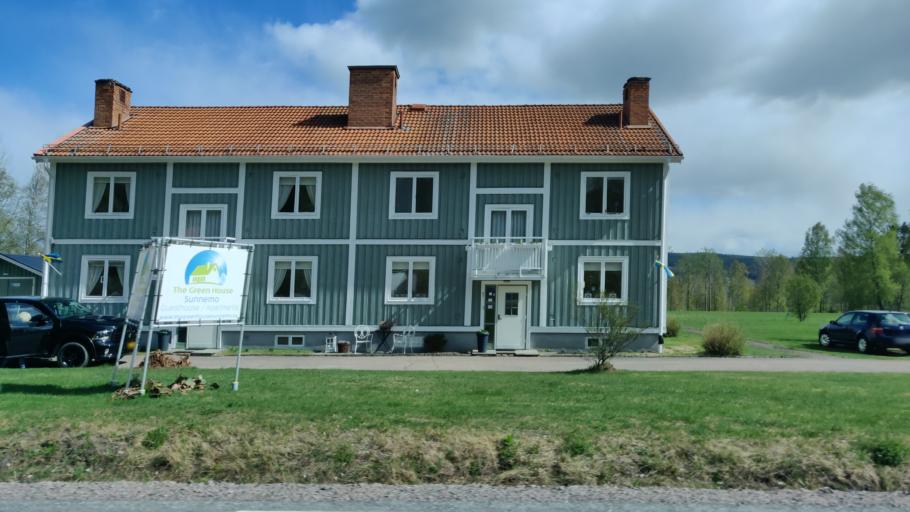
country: SE
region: Vaermland
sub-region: Munkfors Kommun
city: Munkfors
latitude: 59.8543
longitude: 13.7071
